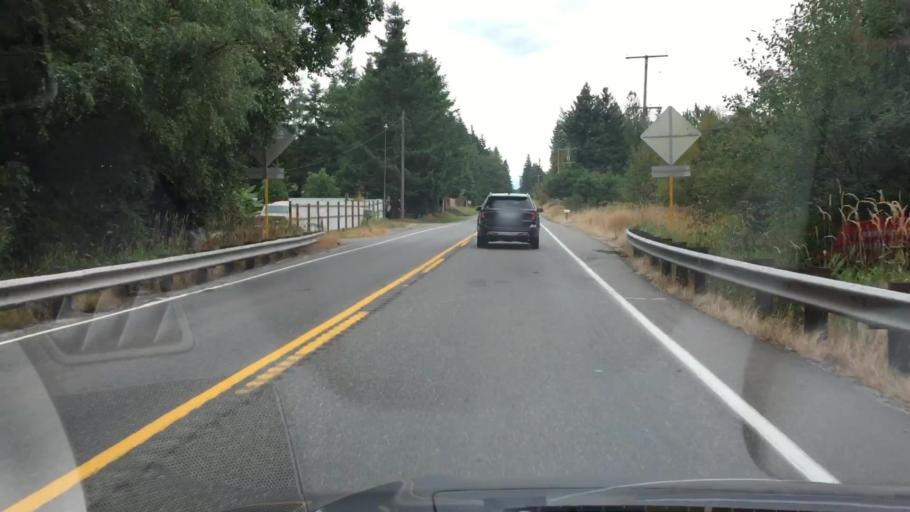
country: US
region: Washington
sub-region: Pierce County
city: Graham
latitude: 46.9936
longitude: -122.2958
